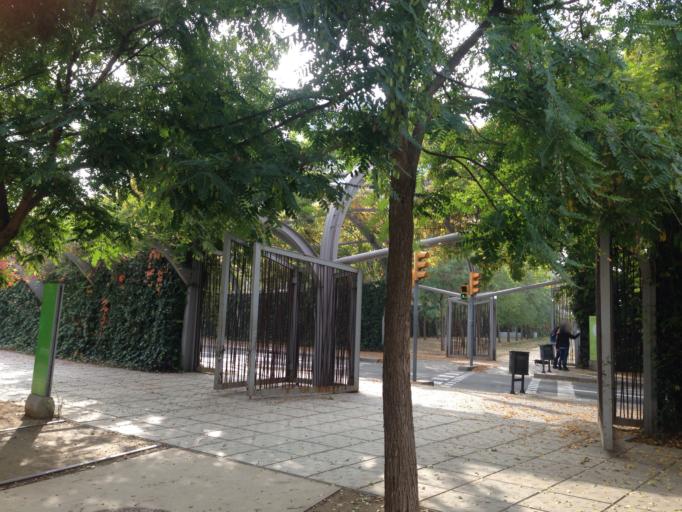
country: ES
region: Catalonia
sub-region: Provincia de Barcelona
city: Sant Marti
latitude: 41.4080
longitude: 2.2016
